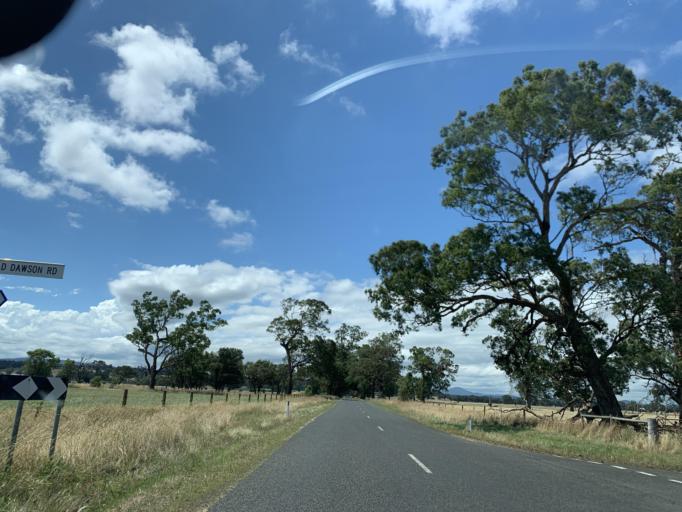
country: AU
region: Victoria
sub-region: Wellington
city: Heyfield
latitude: -37.9799
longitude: 146.6948
